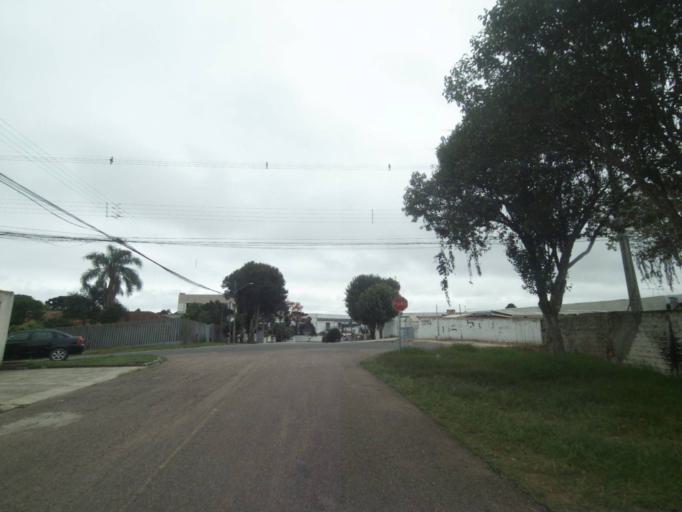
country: BR
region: Parana
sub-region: Sao Jose Dos Pinhais
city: Sao Jose dos Pinhais
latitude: -25.5458
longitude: -49.2837
